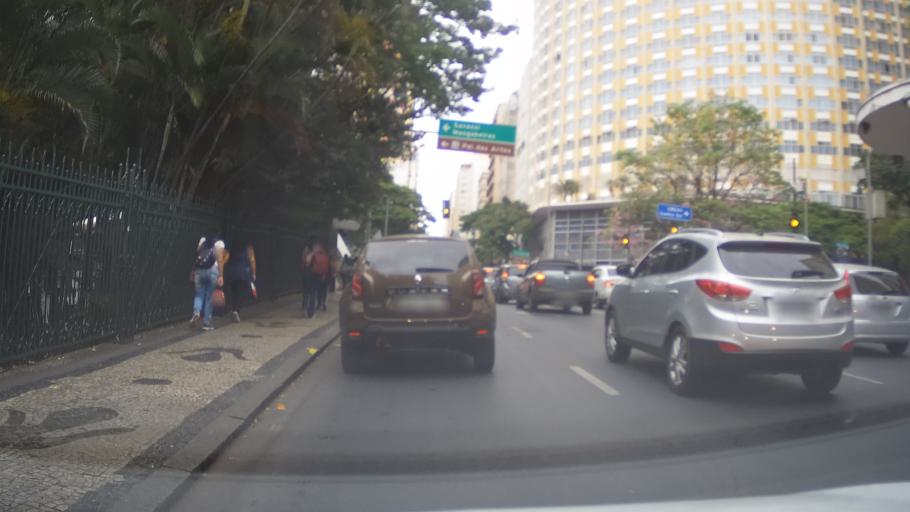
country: BR
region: Minas Gerais
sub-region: Belo Horizonte
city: Belo Horizonte
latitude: -19.9216
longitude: -43.9364
